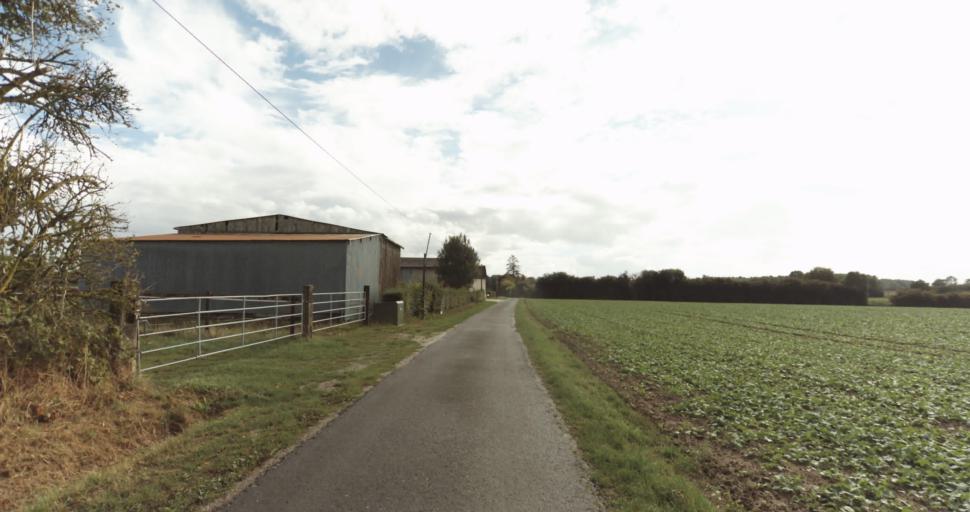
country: FR
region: Lower Normandy
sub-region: Departement de l'Orne
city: Sainte-Gauburge-Sainte-Colombe
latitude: 48.6678
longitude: 0.3822
